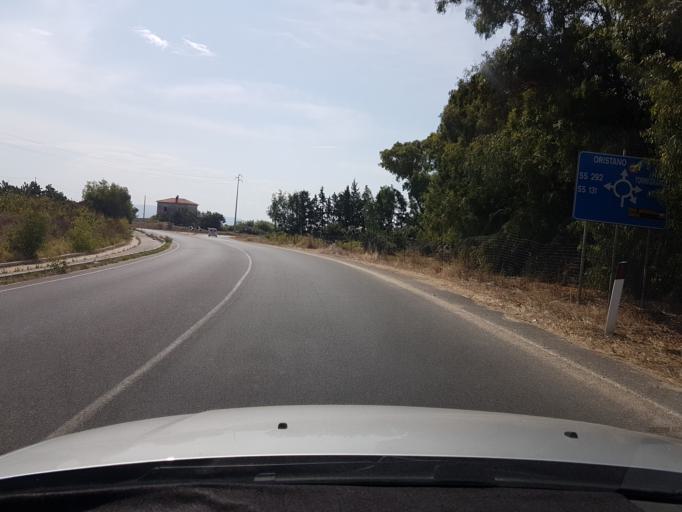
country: IT
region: Sardinia
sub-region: Provincia di Oristano
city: Cabras
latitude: 39.9154
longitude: 8.5409
